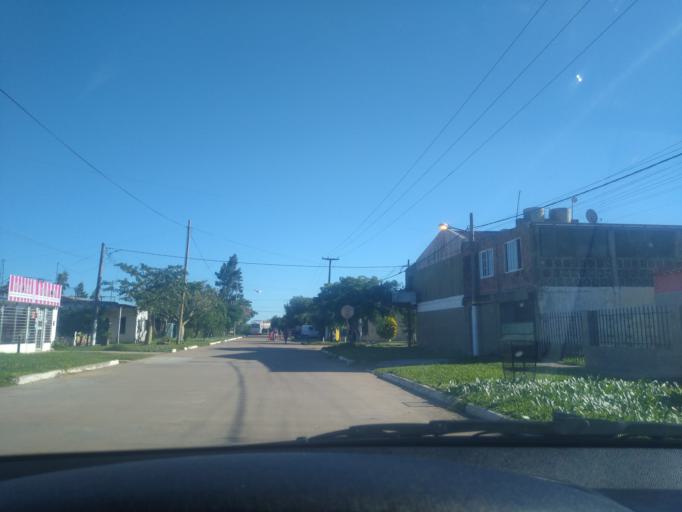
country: AR
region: Chaco
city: Puerto Vilelas
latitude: -27.5178
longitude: -58.9441
